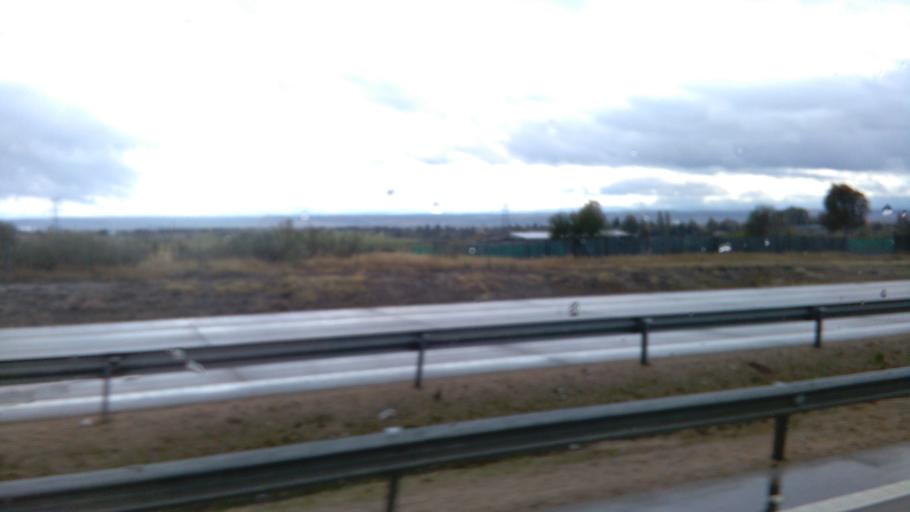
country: ES
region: Castille-La Mancha
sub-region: Province of Toledo
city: Cervera de los Montes
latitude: 40.0140
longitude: -4.8093
